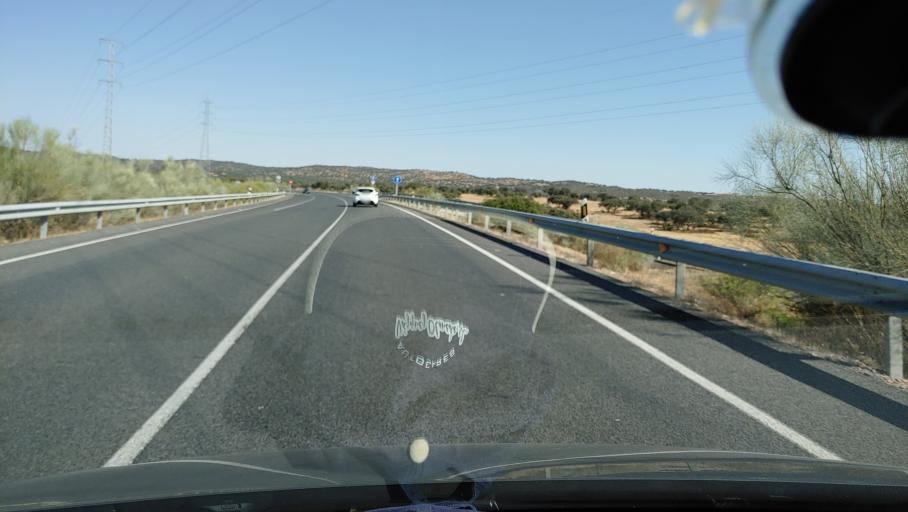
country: ES
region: Andalusia
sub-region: Province of Cordoba
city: Obejo
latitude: 38.0491
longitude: -4.8092
